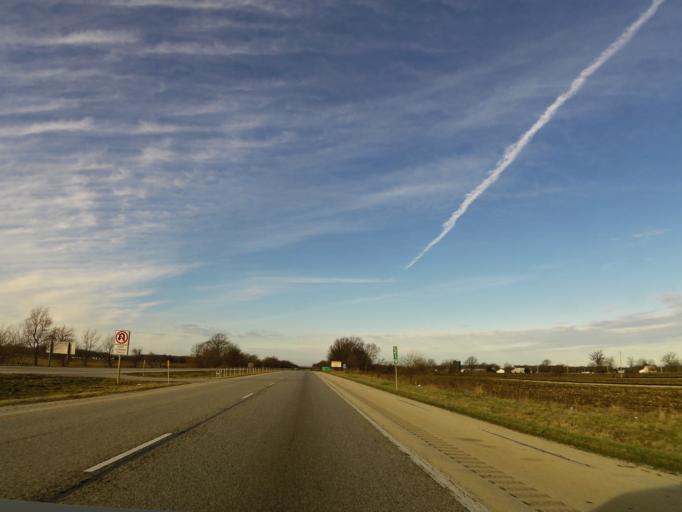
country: US
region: Illinois
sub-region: Vermilion County
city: Danville
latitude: 40.1158
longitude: -87.5511
